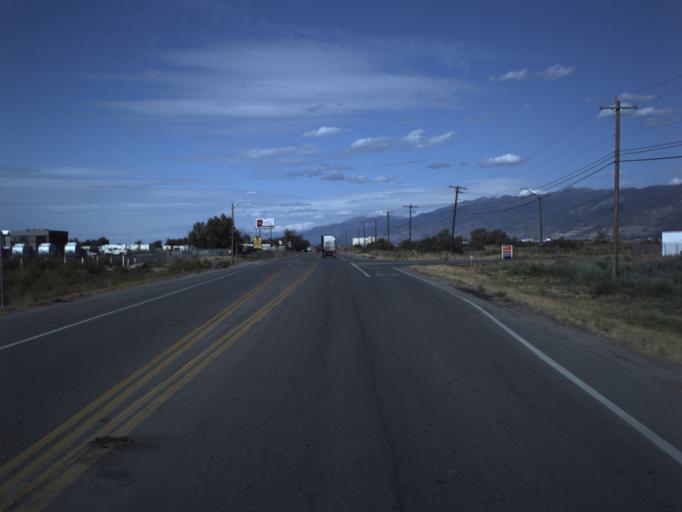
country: US
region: Utah
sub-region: Davis County
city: North Salt Lake
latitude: 40.8159
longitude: -111.9383
